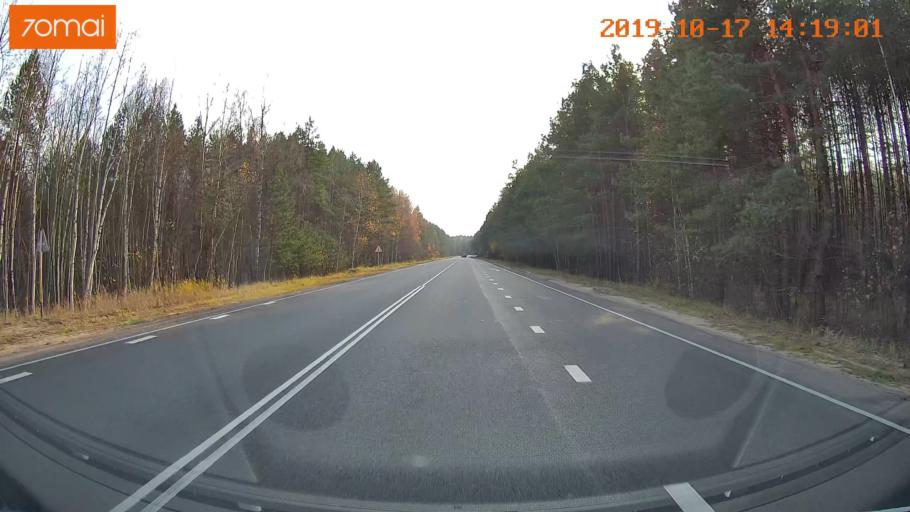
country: RU
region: Rjazan
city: Spas-Klepiki
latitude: 55.0557
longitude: 40.0246
